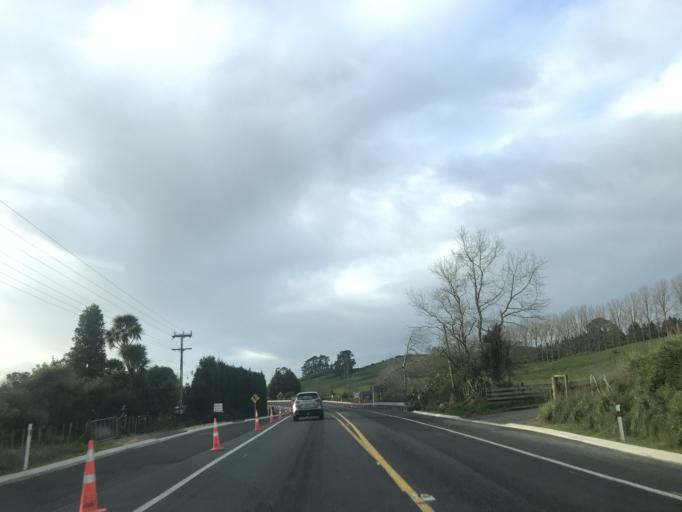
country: NZ
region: Bay of Plenty
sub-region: Western Bay of Plenty District
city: Waihi Beach
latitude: -37.4475
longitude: 175.8784
